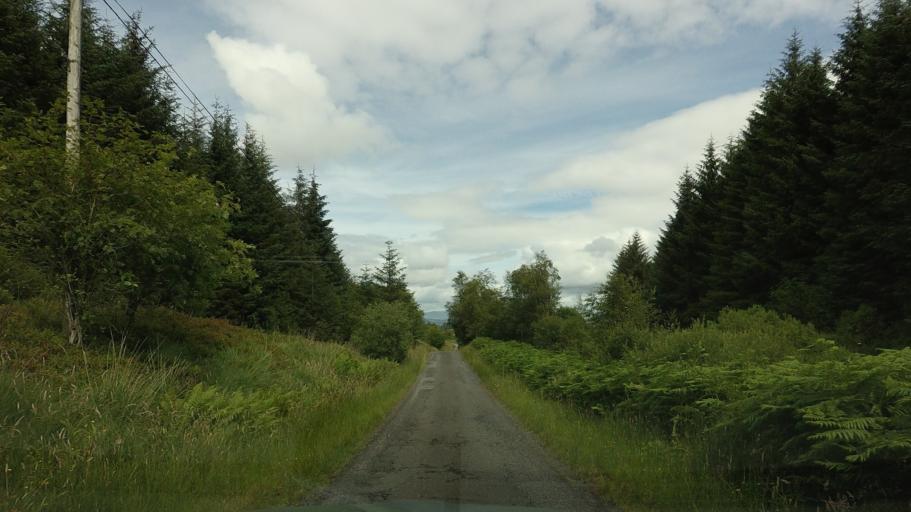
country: GB
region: Scotland
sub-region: Stirling
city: Killearn
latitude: 56.1090
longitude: -4.4086
